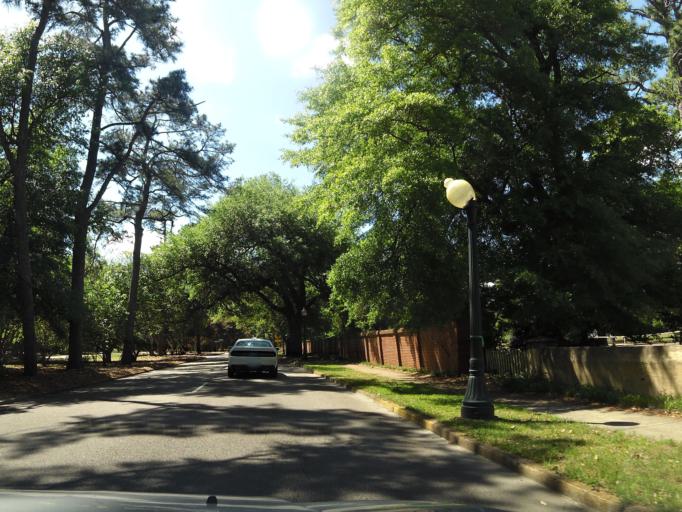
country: US
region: South Carolina
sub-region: Aiken County
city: Aiken
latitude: 33.5633
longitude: -81.7270
